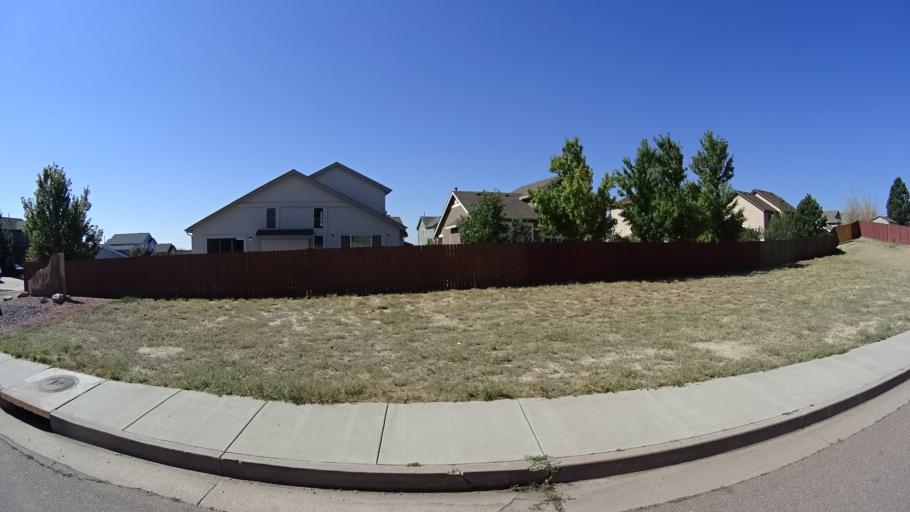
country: US
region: Colorado
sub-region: El Paso County
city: Black Forest
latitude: 38.9441
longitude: -104.7342
